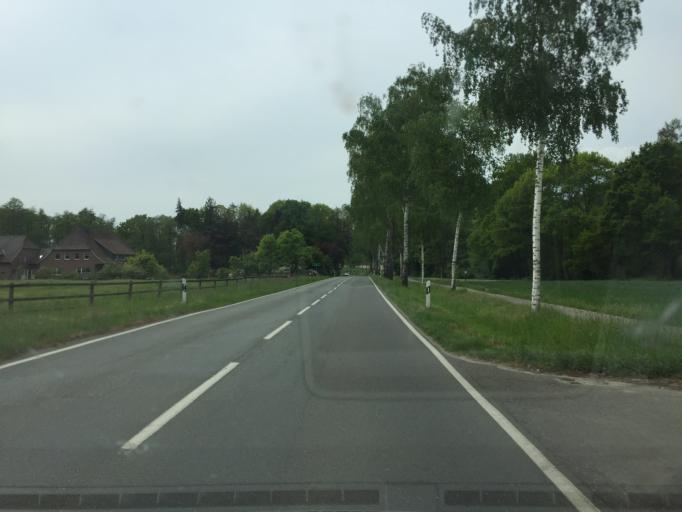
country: DE
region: Lower Saxony
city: Bassum
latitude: 52.8681
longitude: 8.7526
